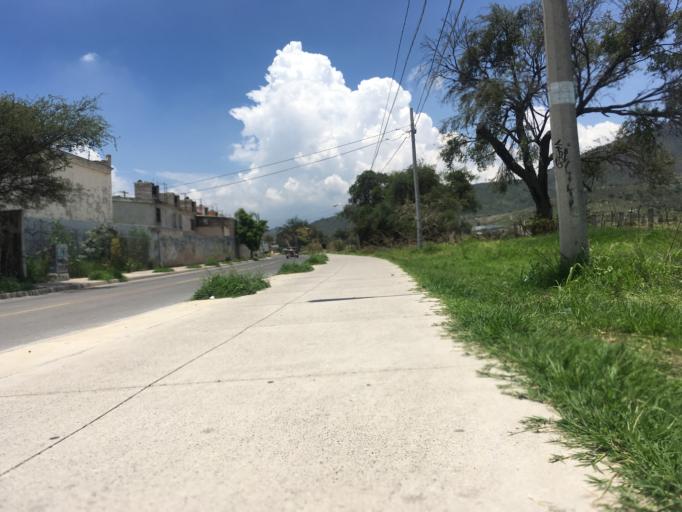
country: MX
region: Jalisco
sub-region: Tlajomulco de Zuniga
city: Jardines de San Sebastian
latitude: 20.5230
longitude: -103.4250
